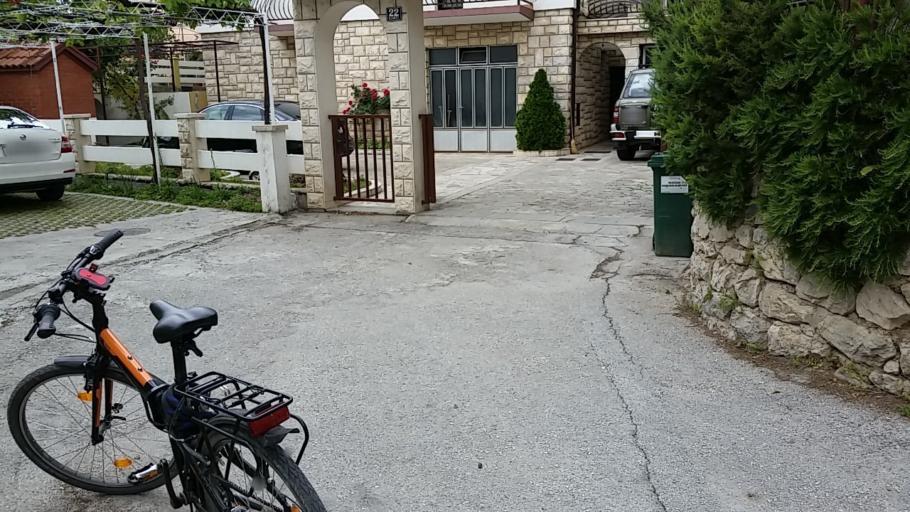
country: HR
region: Splitsko-Dalmatinska
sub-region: Grad Split
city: Stobrec
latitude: 43.5019
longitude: 16.5235
